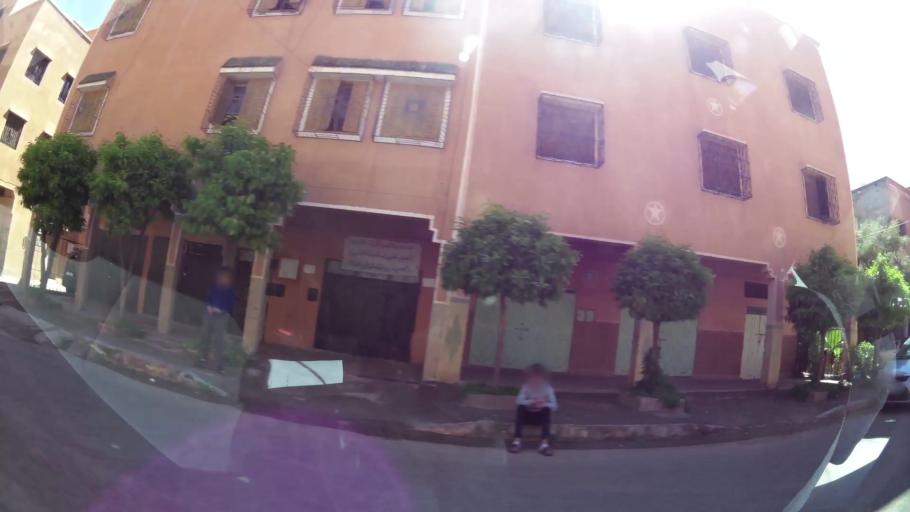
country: MA
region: Marrakech-Tensift-Al Haouz
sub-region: Marrakech
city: Marrakesh
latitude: 31.6363
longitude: -8.0695
